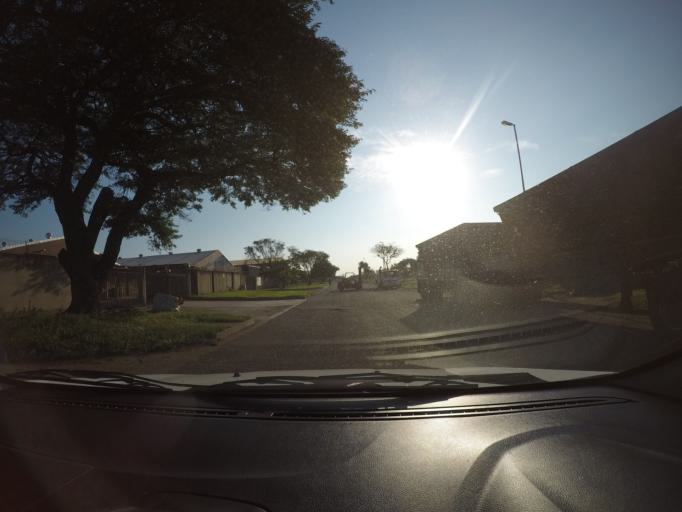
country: ZA
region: KwaZulu-Natal
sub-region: uThungulu District Municipality
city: Richards Bay
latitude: -28.7630
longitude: 32.0061
